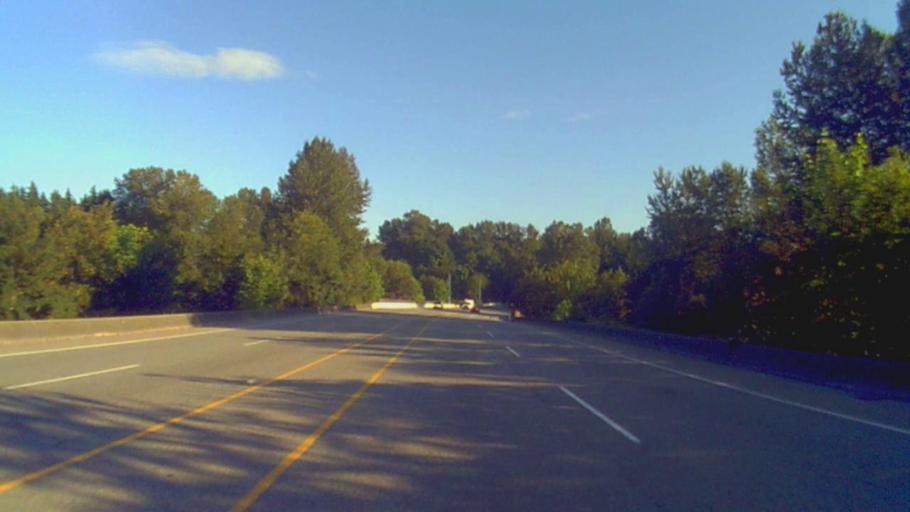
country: CA
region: British Columbia
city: New Westminster
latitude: 49.2484
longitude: -122.9129
